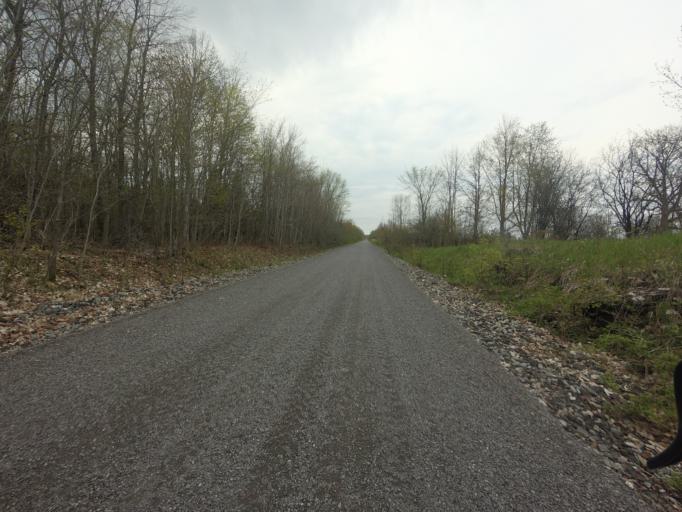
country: CA
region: Ontario
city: Carleton Place
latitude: 45.2093
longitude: -76.1752
